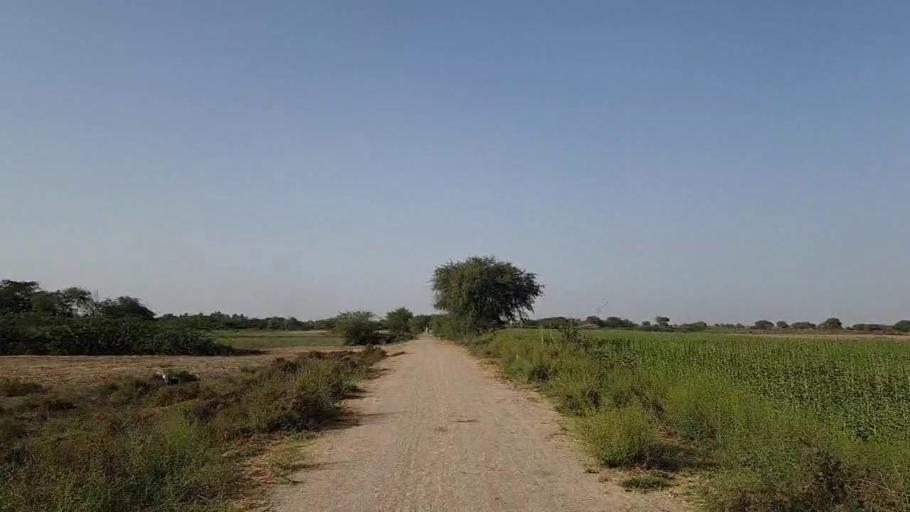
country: PK
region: Sindh
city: Jati
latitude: 24.2885
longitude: 68.1491
